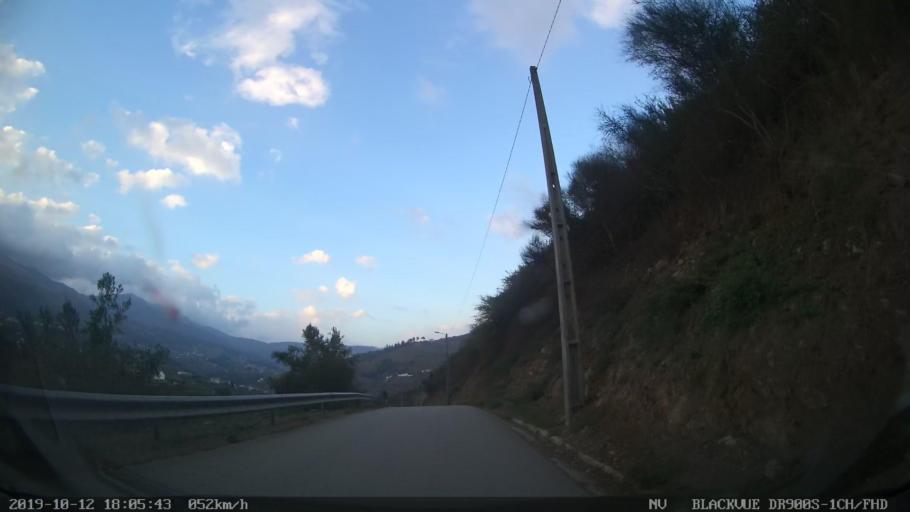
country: PT
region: Vila Real
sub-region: Mesao Frio
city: Mesao Frio
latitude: 41.1786
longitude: -7.8453
